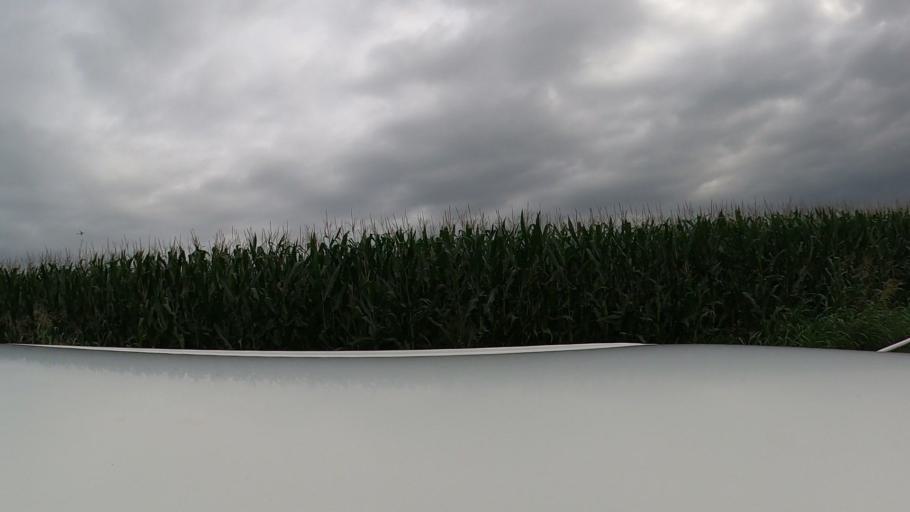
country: JP
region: Kumamoto
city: Ozu
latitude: 32.8380
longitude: 130.8989
